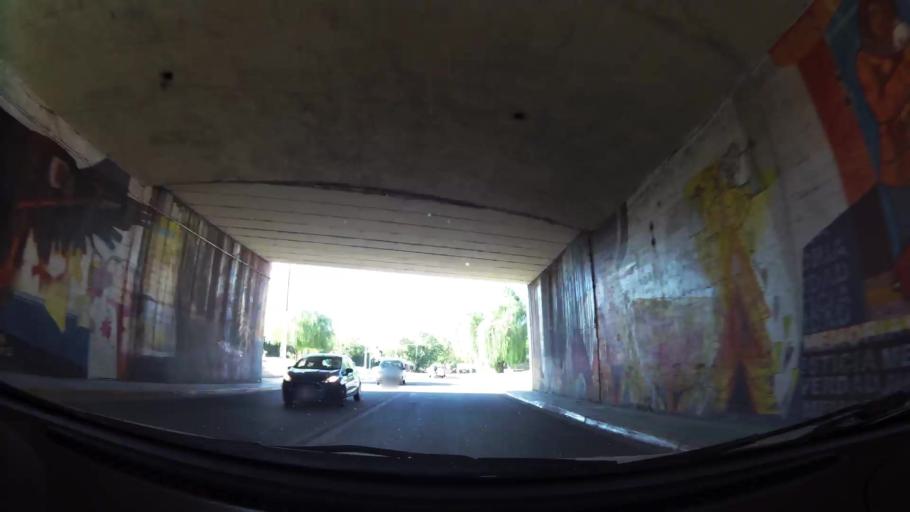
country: AR
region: Mendoza
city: Mendoza
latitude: -32.8978
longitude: -68.8108
